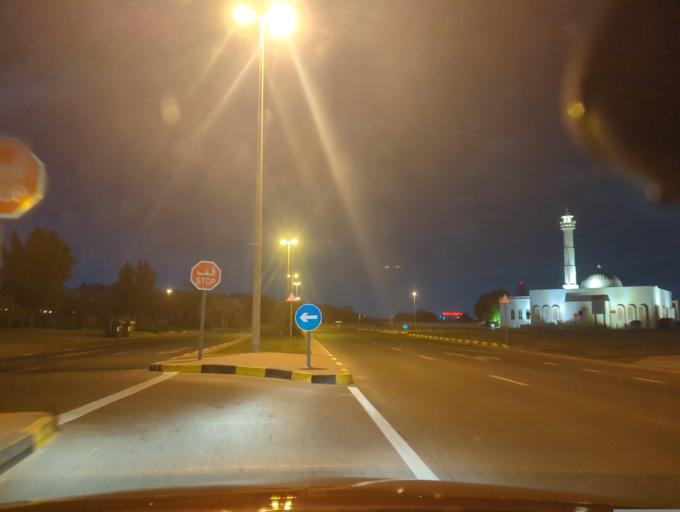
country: AE
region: Ash Shariqah
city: Sharjah
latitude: 25.3584
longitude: 55.4698
